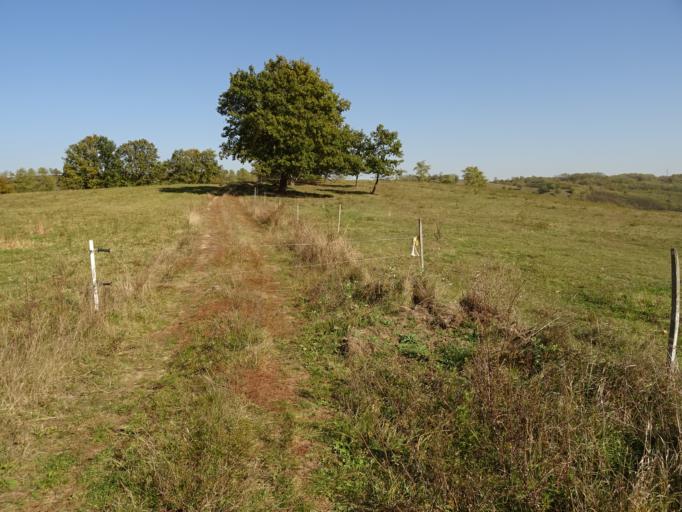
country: HU
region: Nograd
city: Salgotarjan
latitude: 48.0727
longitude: 19.7491
